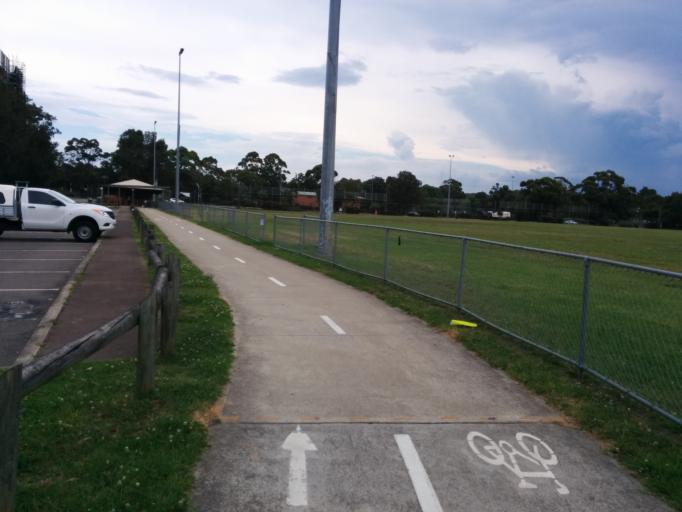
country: AU
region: New South Wales
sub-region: Sutherland Shire
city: Caringbah
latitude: -34.0373
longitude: 151.1378
